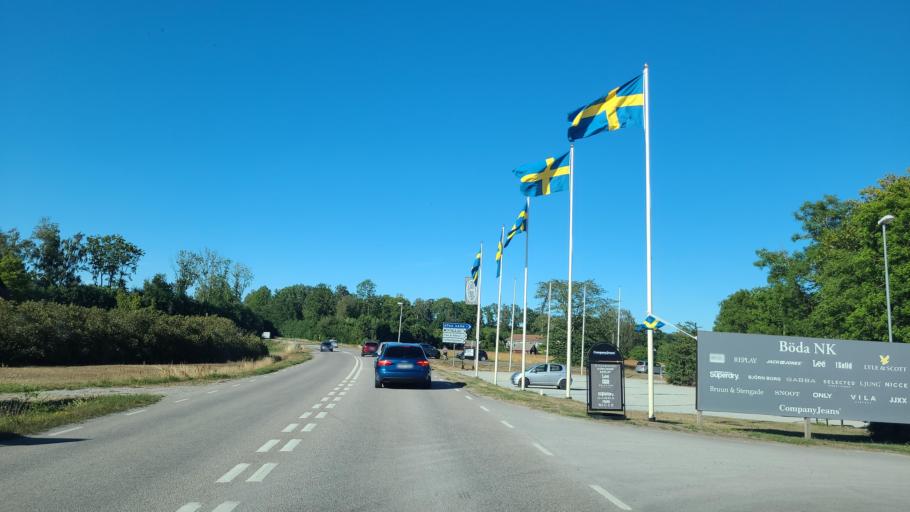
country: SE
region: Kalmar
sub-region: Borgholms Kommun
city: Borgholm
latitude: 57.2369
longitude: 17.0583
